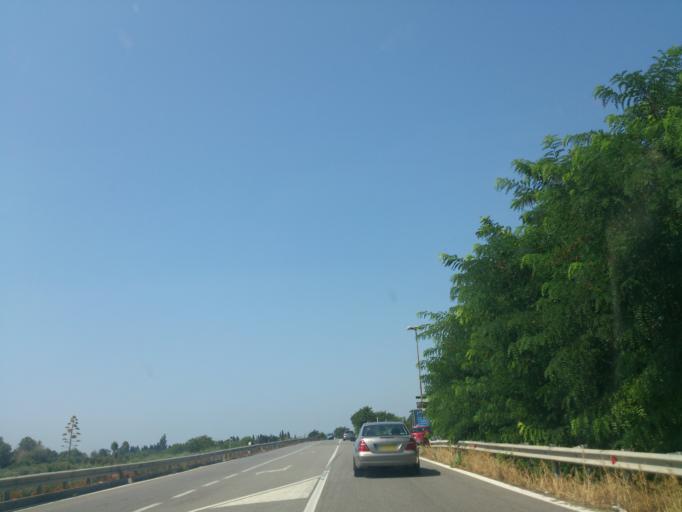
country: IT
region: Calabria
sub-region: Provincia di Reggio Calabria
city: Caulonia Marina
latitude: 38.3576
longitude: 16.4865
